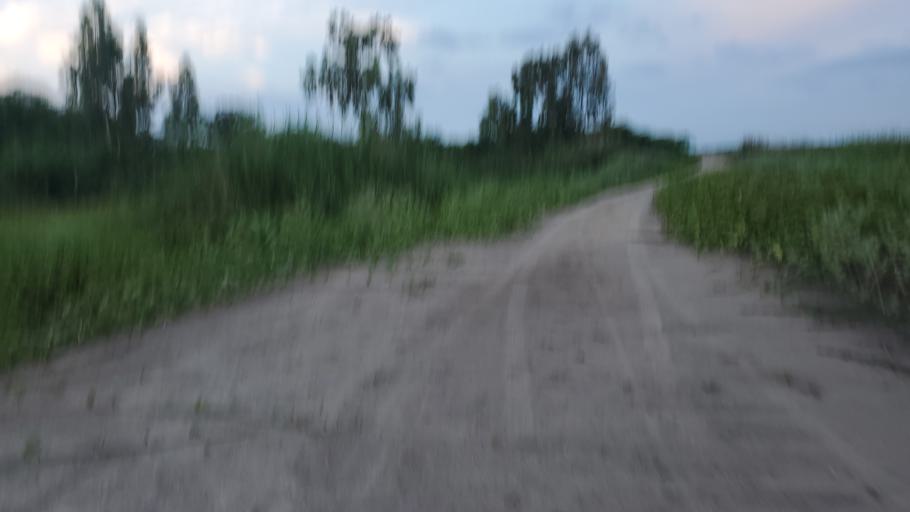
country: SN
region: Saint-Louis
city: Saint-Louis
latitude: 16.0376
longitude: -16.4171
